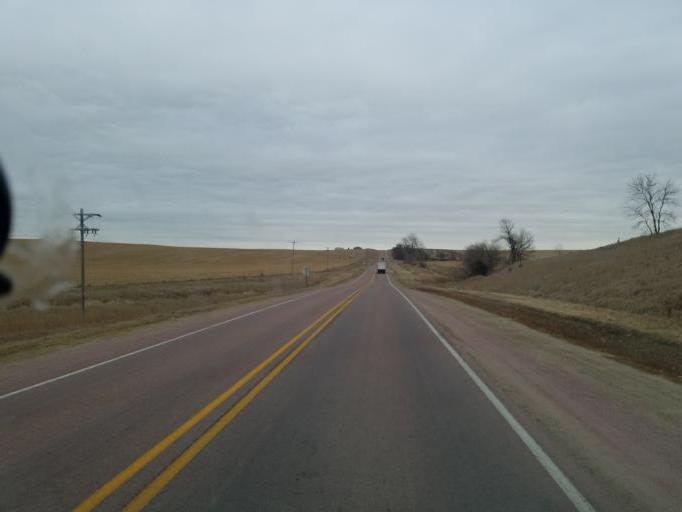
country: US
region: Nebraska
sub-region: Cedar County
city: Hartington
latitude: 42.4675
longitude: -97.2102
